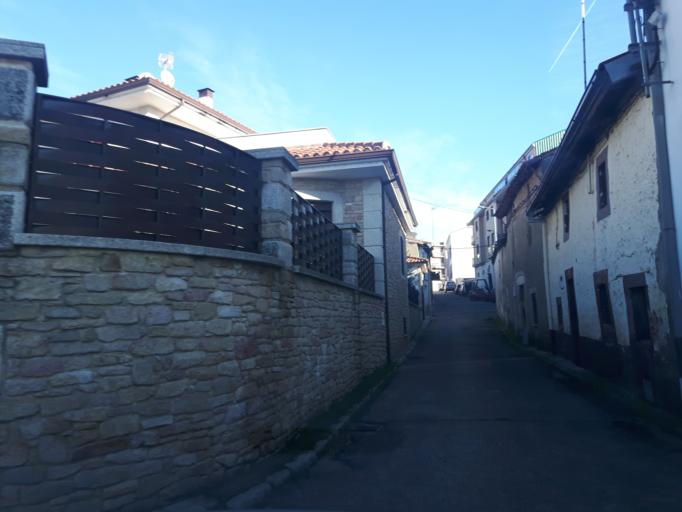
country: ES
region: Castille and Leon
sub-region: Provincia de Salamanca
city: Vitigudino
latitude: 41.0074
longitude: -6.4368
